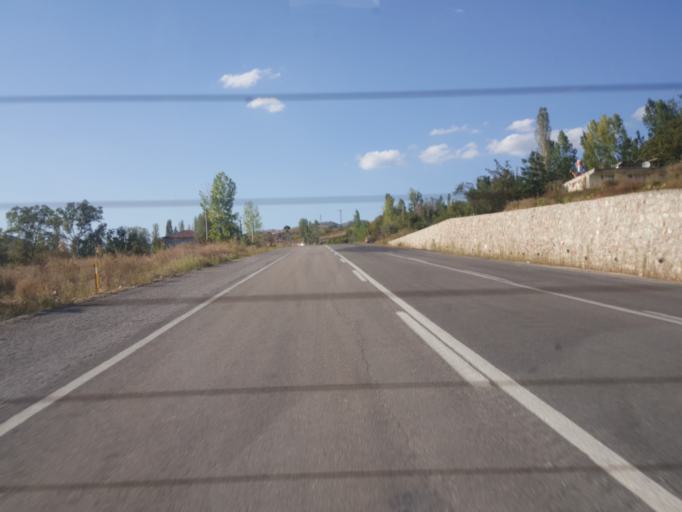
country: TR
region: Amasya
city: Tasova
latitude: 40.7617
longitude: 36.2828
